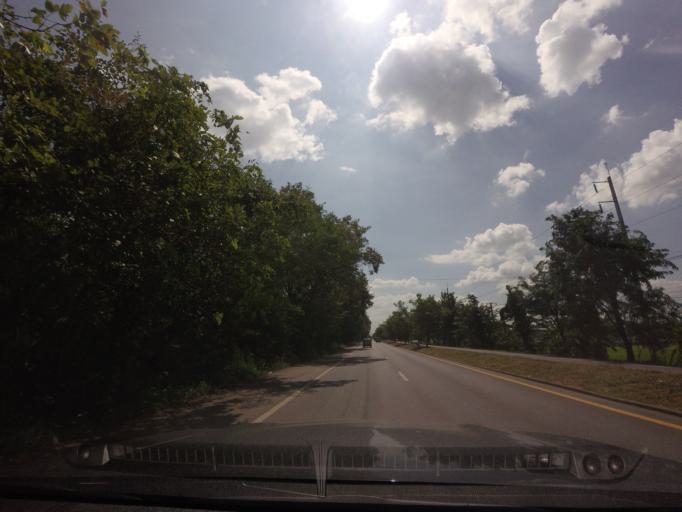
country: TH
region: Phetchabun
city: Nong Phai
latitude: 15.9494
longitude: 101.0367
